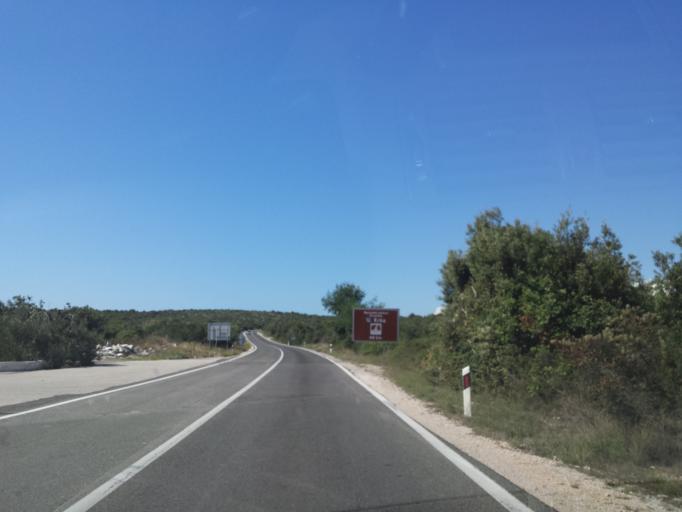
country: HR
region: Sibensko-Kniniska
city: Rogoznica
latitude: 43.5428
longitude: 15.9667
